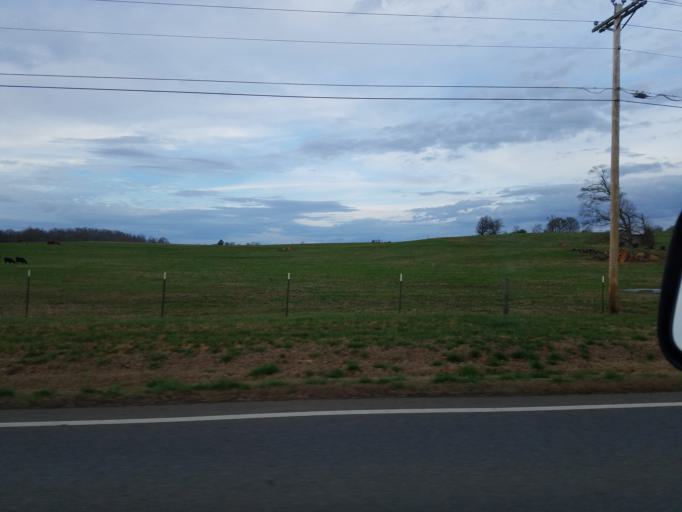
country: US
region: Georgia
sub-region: Gordon County
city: Calhoun
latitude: 34.4488
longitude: -84.8592
